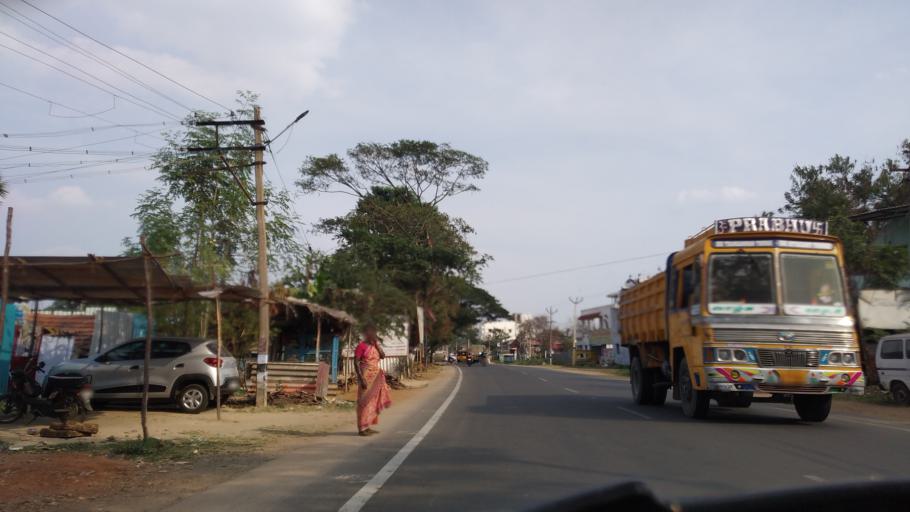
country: IN
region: Tamil Nadu
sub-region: Coimbatore
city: Perur
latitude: 10.9695
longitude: 76.8975
